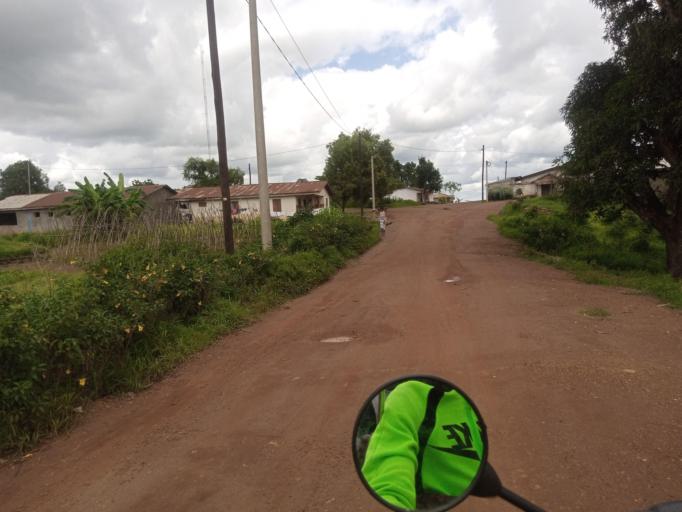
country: SL
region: Northern Province
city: Port Loko
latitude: 8.7622
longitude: -12.7801
